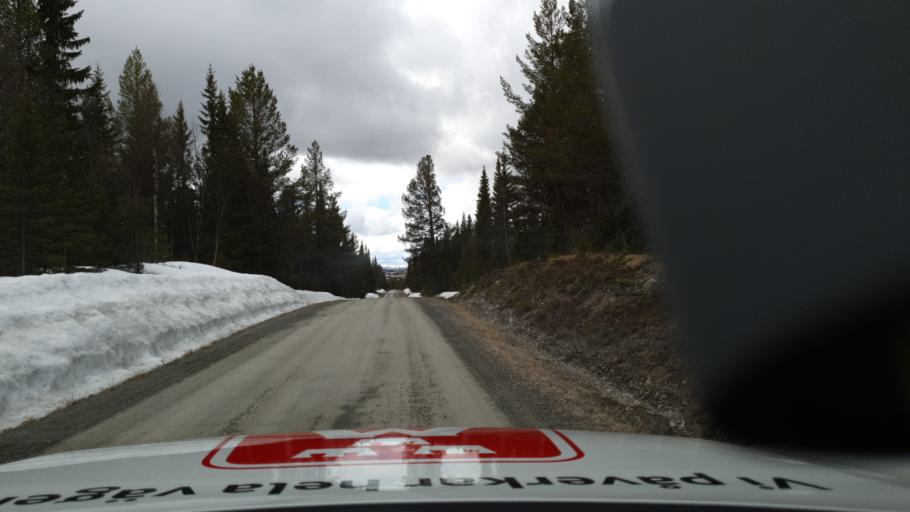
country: SE
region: Jaemtland
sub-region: Are Kommun
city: Jarpen
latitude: 62.8265
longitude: 13.8176
